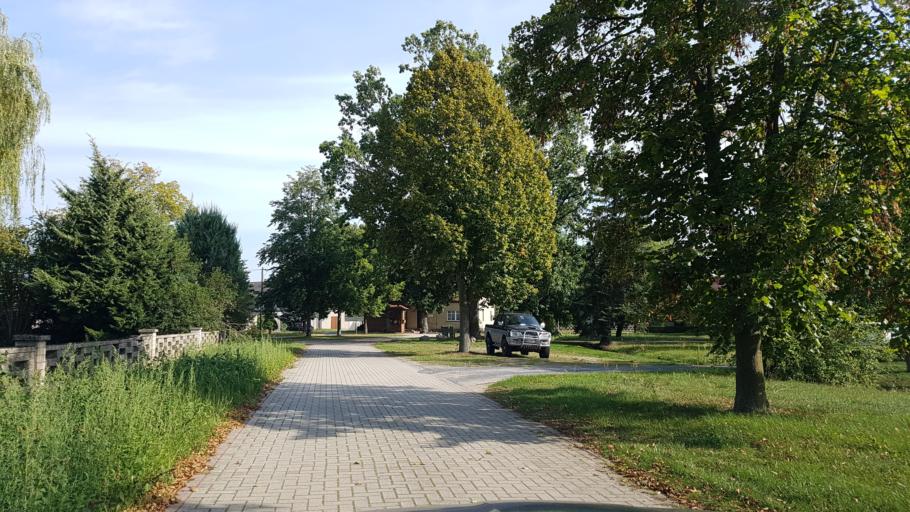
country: DE
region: Brandenburg
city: Schilda
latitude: 51.6284
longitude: 13.3184
